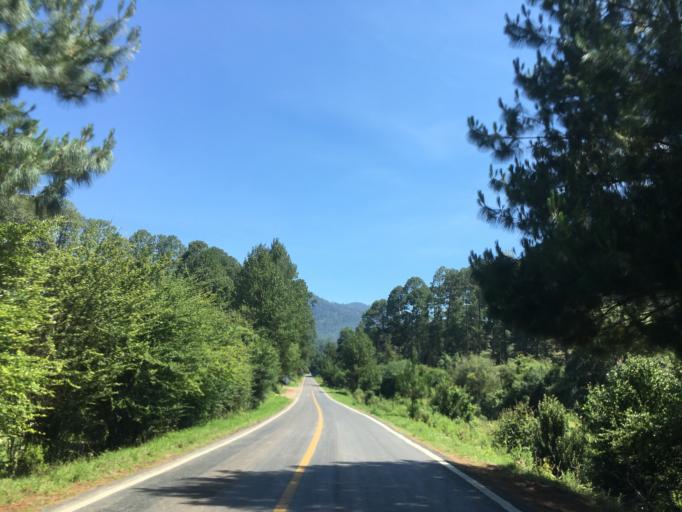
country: MX
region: Michoacan
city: Tzitzio
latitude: 19.6266
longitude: -100.7734
